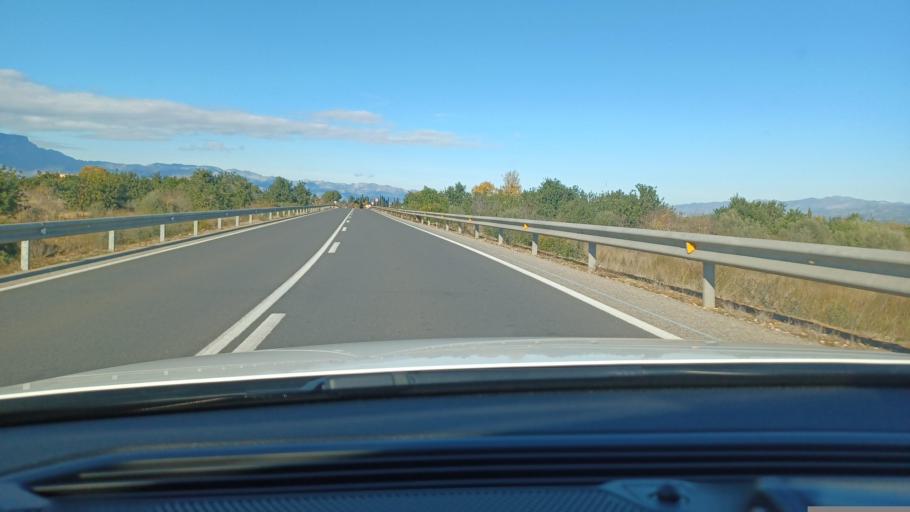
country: ES
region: Catalonia
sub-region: Provincia de Tarragona
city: Santa Barbara
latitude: 40.7196
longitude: 0.5056
